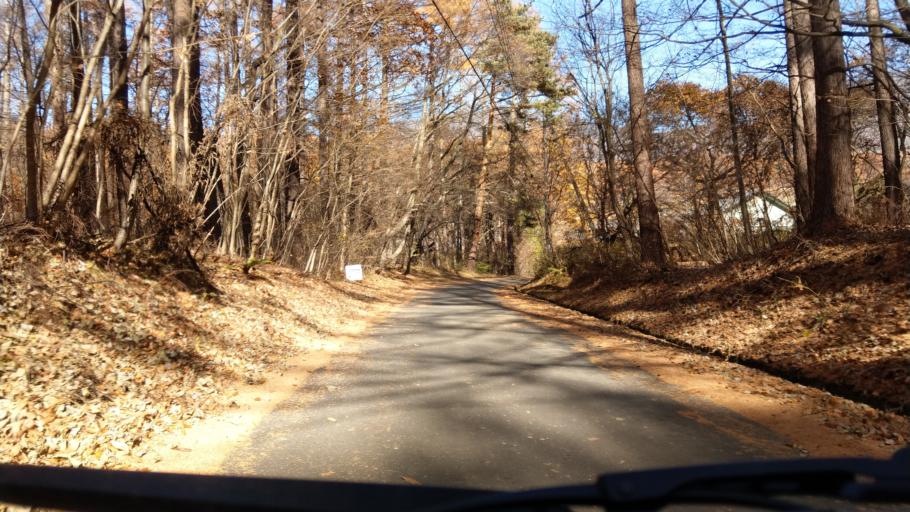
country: JP
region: Nagano
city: Komoro
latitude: 36.3568
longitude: 138.4549
